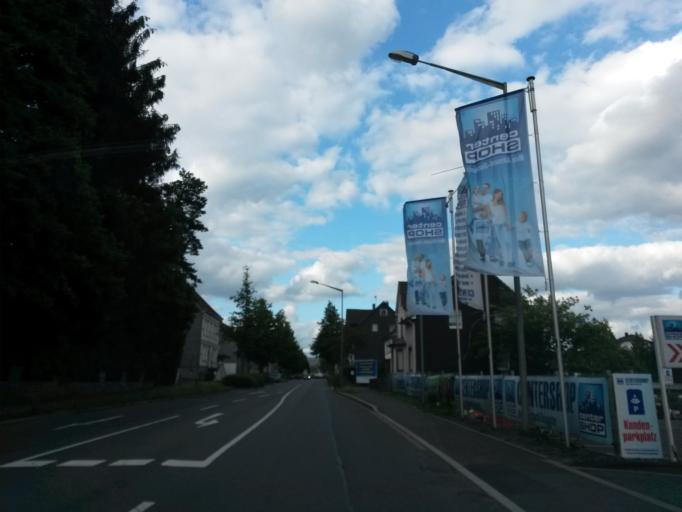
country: DE
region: North Rhine-Westphalia
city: Bergneustadt
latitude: 51.0121
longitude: 7.6322
